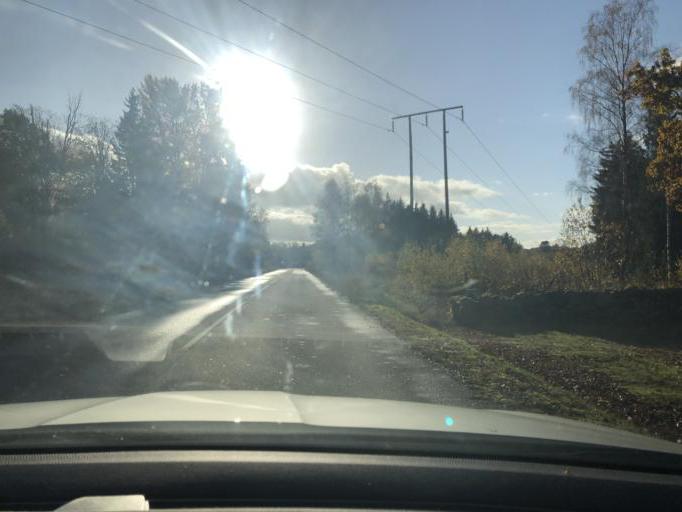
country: SE
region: Vaestra Goetaland
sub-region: Ulricehamns Kommun
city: Ulricehamn
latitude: 57.8161
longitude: 13.2918
